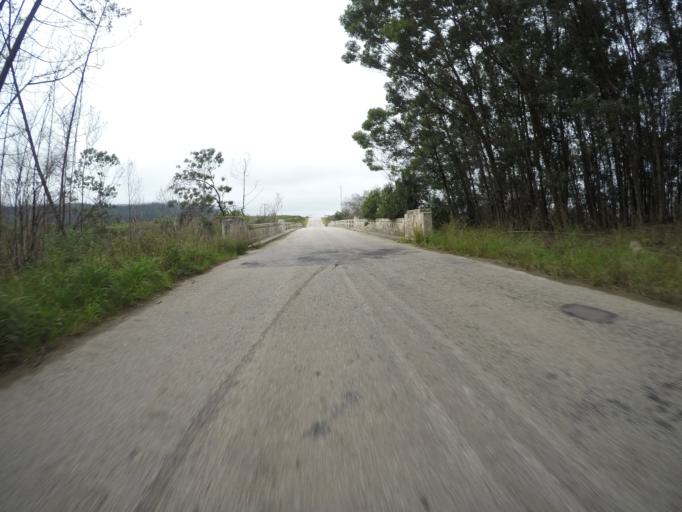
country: ZA
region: Eastern Cape
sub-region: Cacadu District Municipality
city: Kareedouw
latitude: -33.9814
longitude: 24.0495
